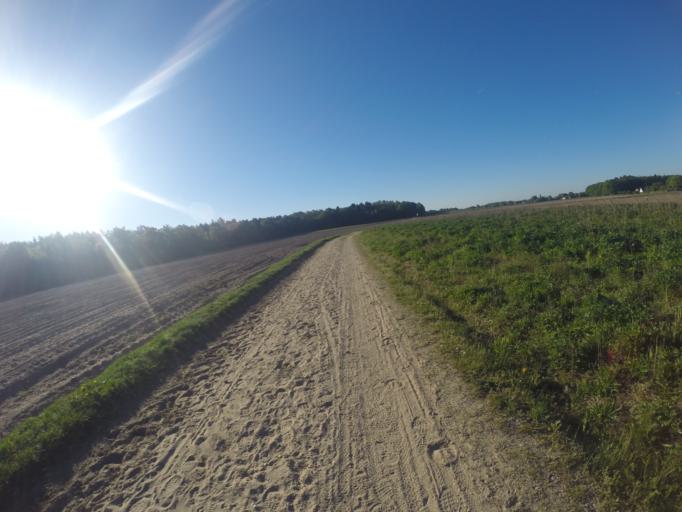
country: NL
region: Gelderland
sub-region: Gemeente Montferland
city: s-Heerenberg
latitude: 51.8912
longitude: 6.2309
